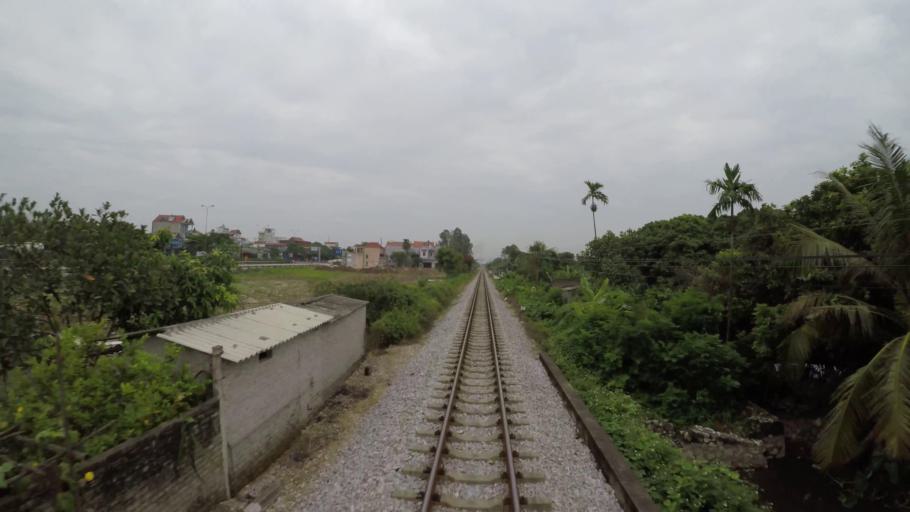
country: VN
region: Hai Duong
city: Nam Sach
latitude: 20.9773
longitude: 106.4089
